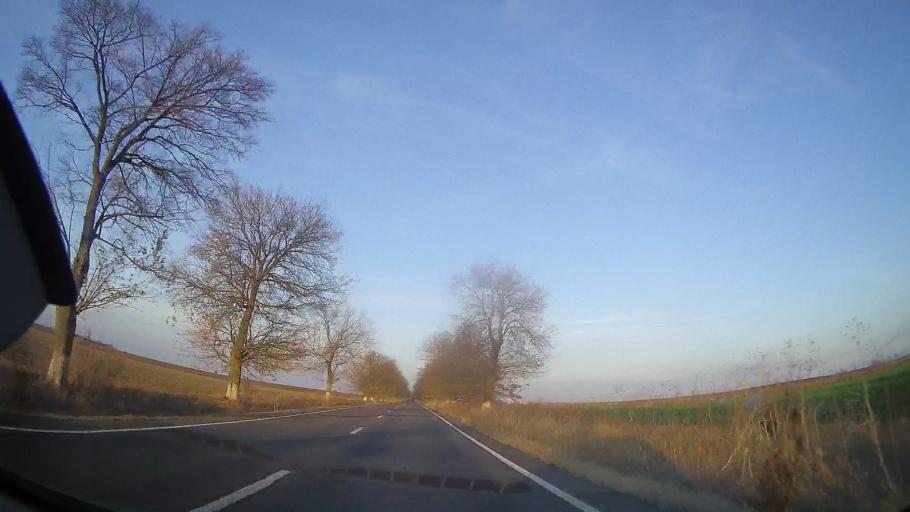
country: RO
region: Constanta
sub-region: Comuna Amzacea
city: Amzacea
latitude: 43.9498
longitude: 28.3812
